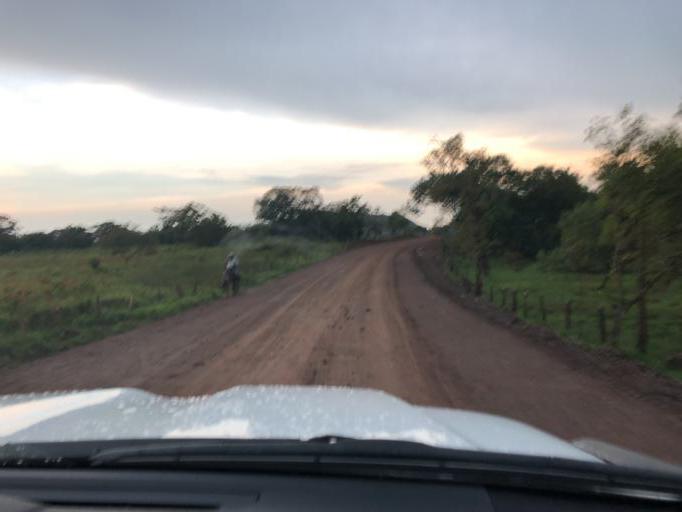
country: NI
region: Chontales
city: La Libertad
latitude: 12.1905
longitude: -85.1745
